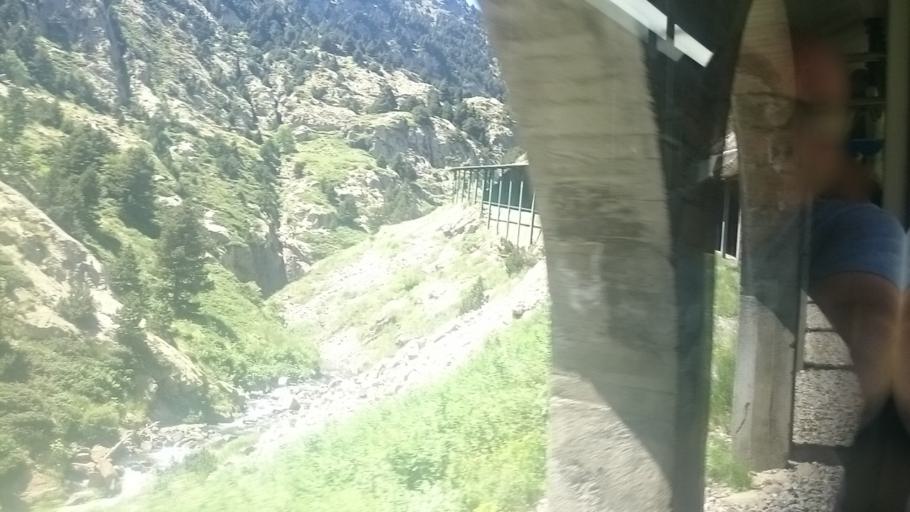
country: ES
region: Catalonia
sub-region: Provincia de Girona
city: Ribes de Freser
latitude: 42.3902
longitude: 2.1557
